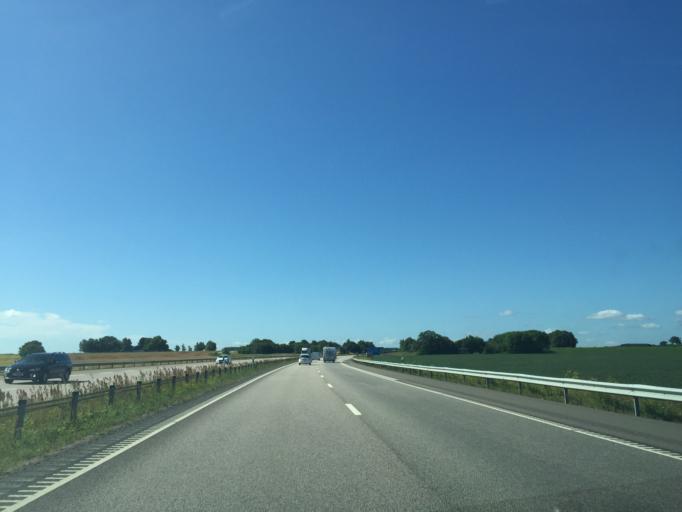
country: SE
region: Skane
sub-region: Helsingborg
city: Hyllinge
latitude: 56.1084
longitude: 12.8086
